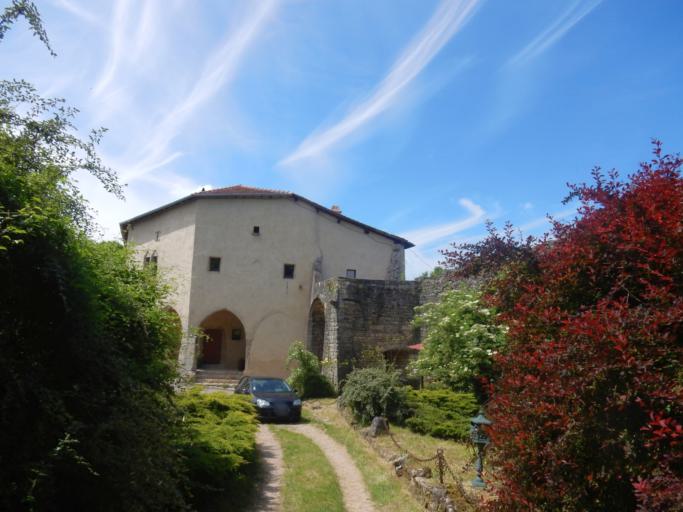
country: FR
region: Lorraine
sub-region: Departement de Meurthe-et-Moselle
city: Pagny-sur-Moselle
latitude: 48.9790
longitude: 5.9953
